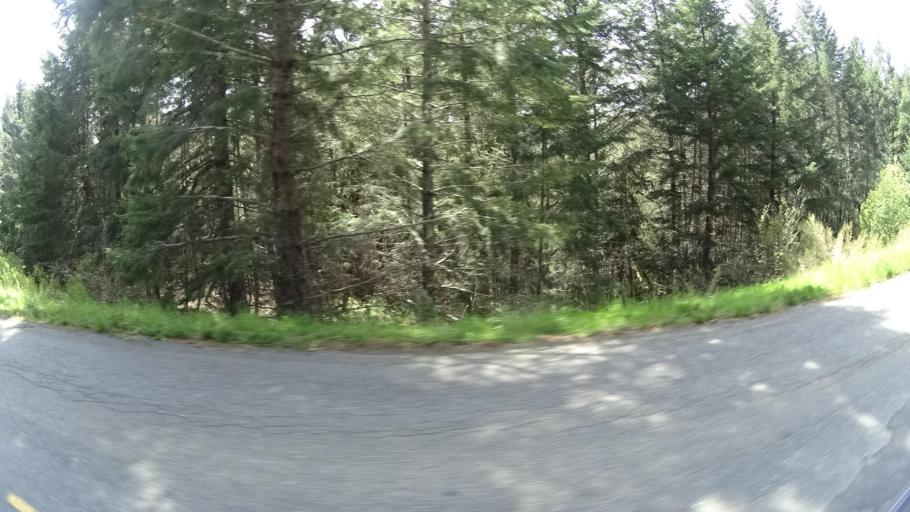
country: US
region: California
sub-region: Humboldt County
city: Redway
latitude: 40.4085
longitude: -123.7556
